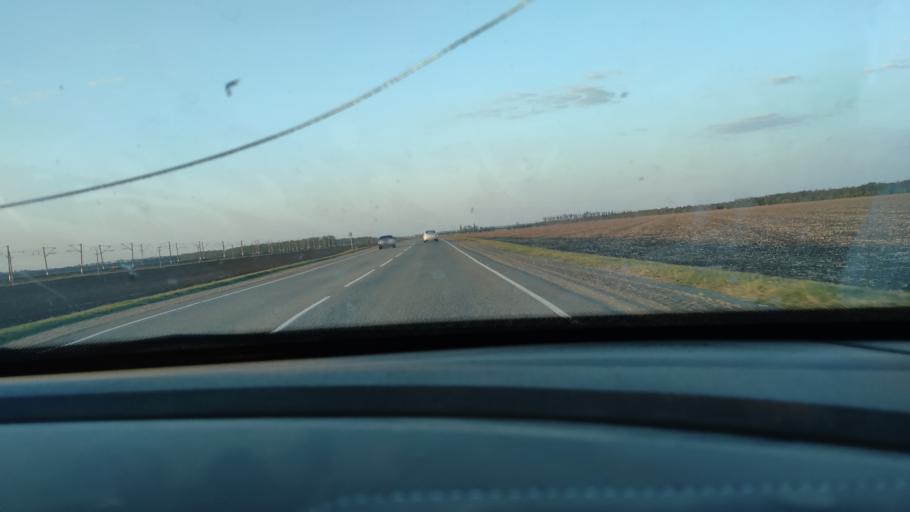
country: RU
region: Krasnodarskiy
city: Novominskaya
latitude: 46.3488
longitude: 38.9596
